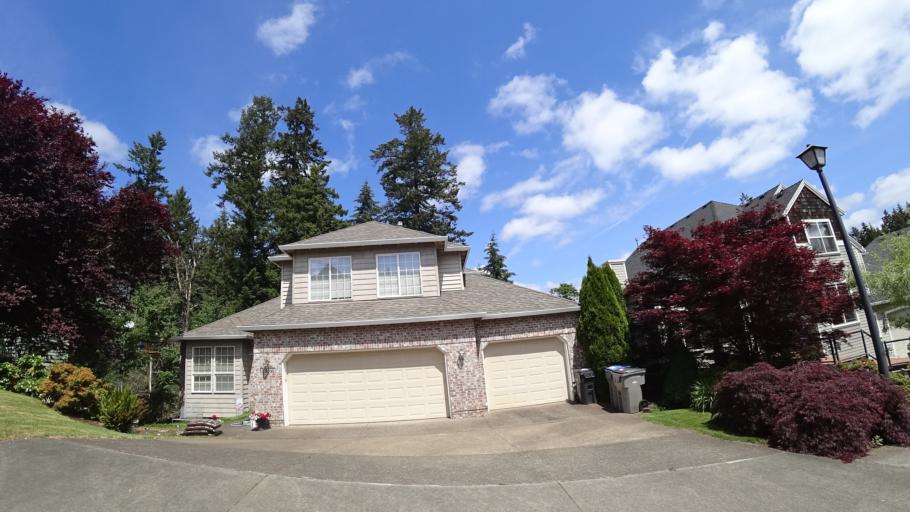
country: US
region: Oregon
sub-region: Washington County
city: King City
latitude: 45.4254
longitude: -122.8167
